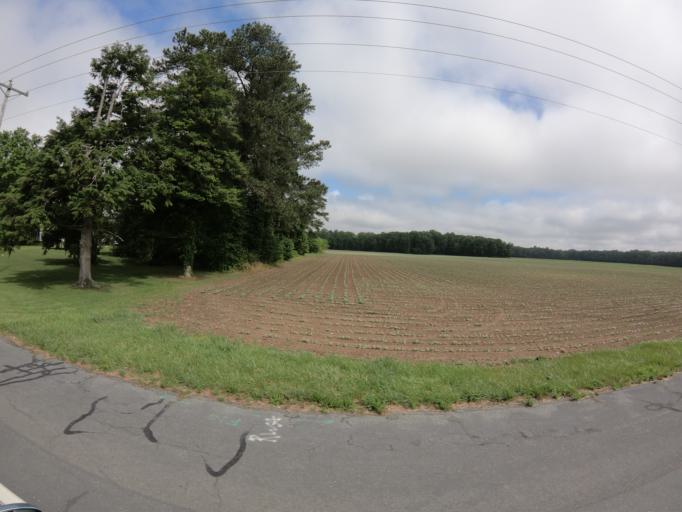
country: US
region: Delaware
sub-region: Kent County
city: Riverview
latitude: 39.0077
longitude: -75.5234
